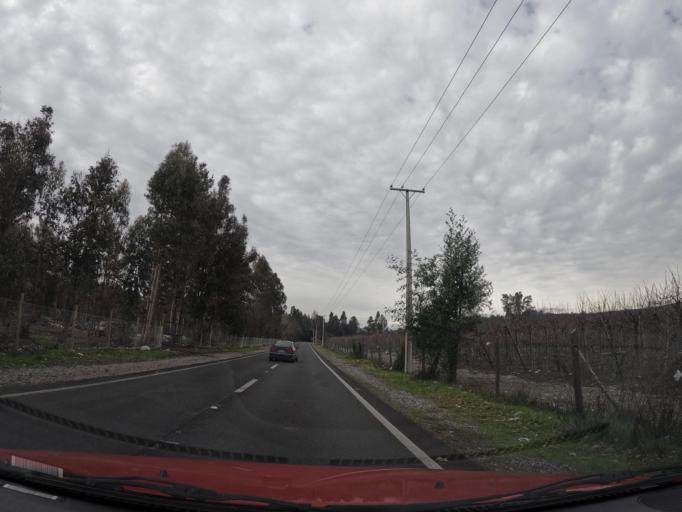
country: CL
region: Maule
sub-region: Provincia de Linares
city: Linares
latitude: -35.9124
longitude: -71.4918
